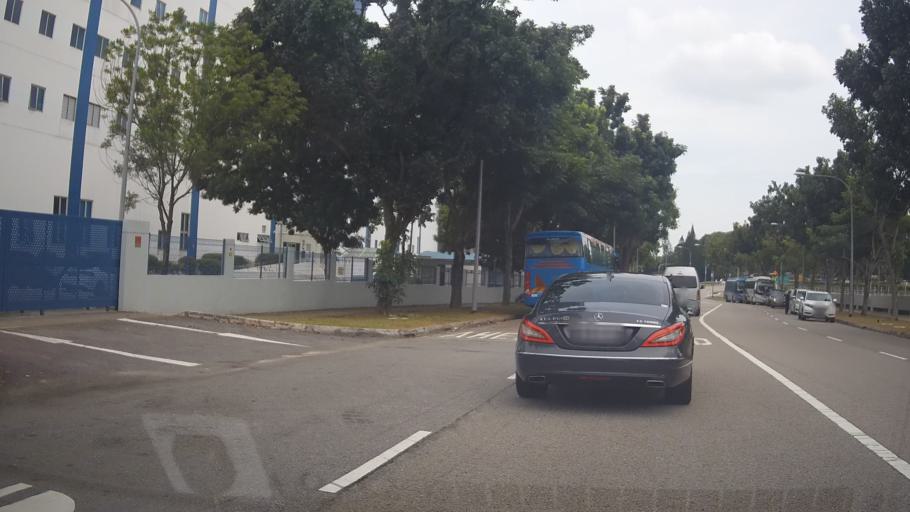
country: SG
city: Singapore
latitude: 1.3467
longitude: 103.9678
